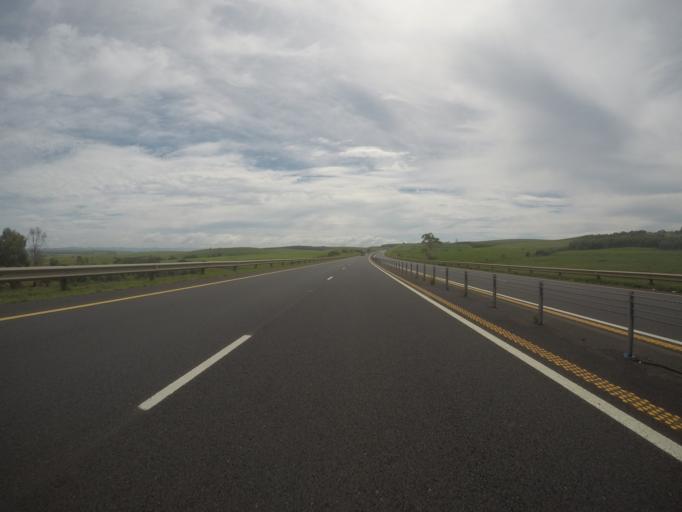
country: ZA
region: KwaZulu-Natal
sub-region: uThungulu District Municipality
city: Eshowe
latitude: -29.0549
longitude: 31.6320
